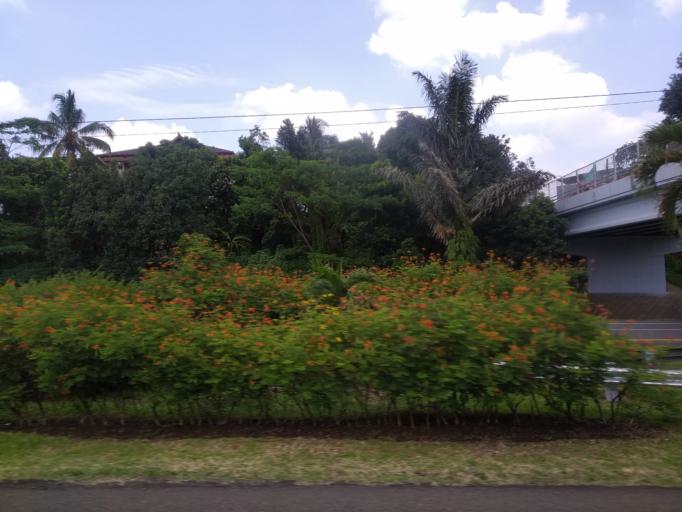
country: ID
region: West Java
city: Bogor
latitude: -6.6003
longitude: 106.8132
